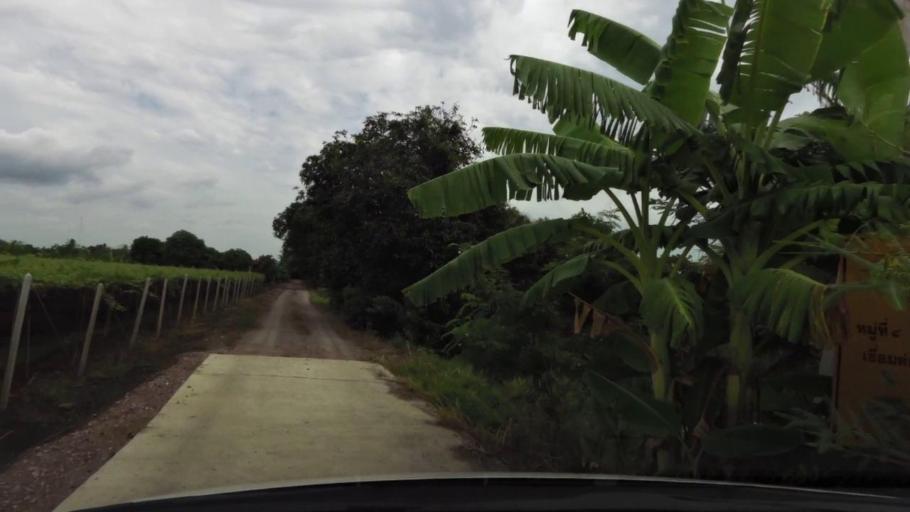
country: TH
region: Ratchaburi
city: Damnoen Saduak
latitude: 13.5522
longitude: 99.9761
